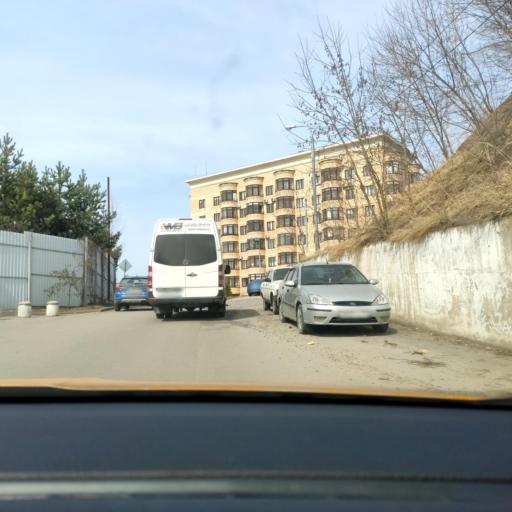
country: RU
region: Moskovskaya
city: Skhodnya
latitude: 55.9408
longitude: 37.3194
